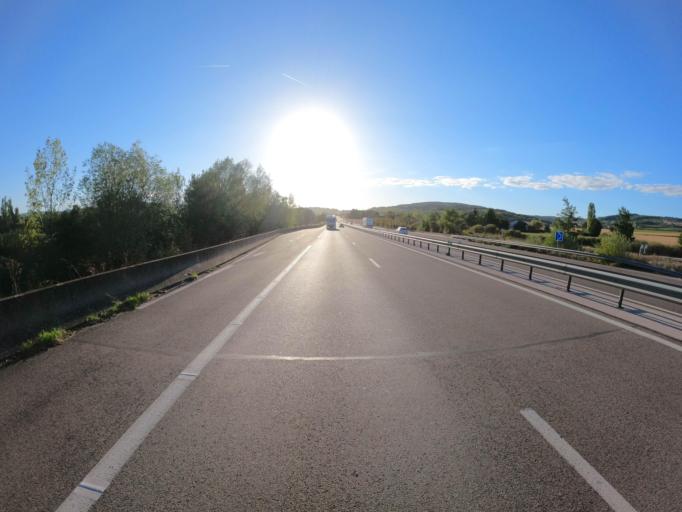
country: FR
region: Bourgogne
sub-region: Departement de Saone-et-Loire
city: Givry
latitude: 46.7585
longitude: 4.7306
